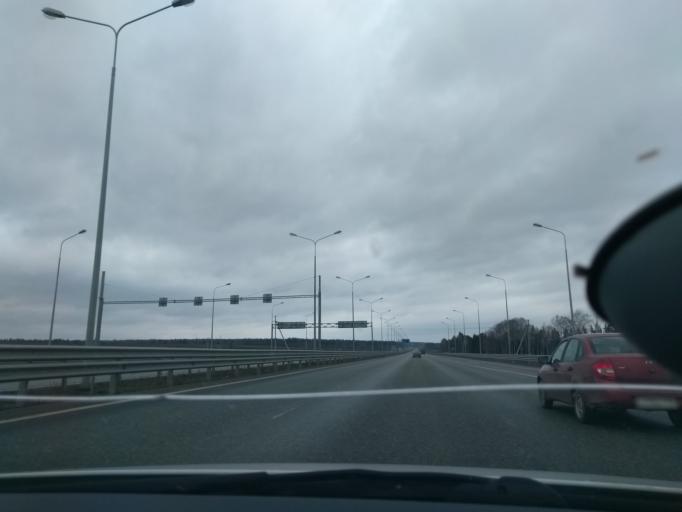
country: RU
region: Perm
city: Bershet'
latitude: 57.6837
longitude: 56.4217
